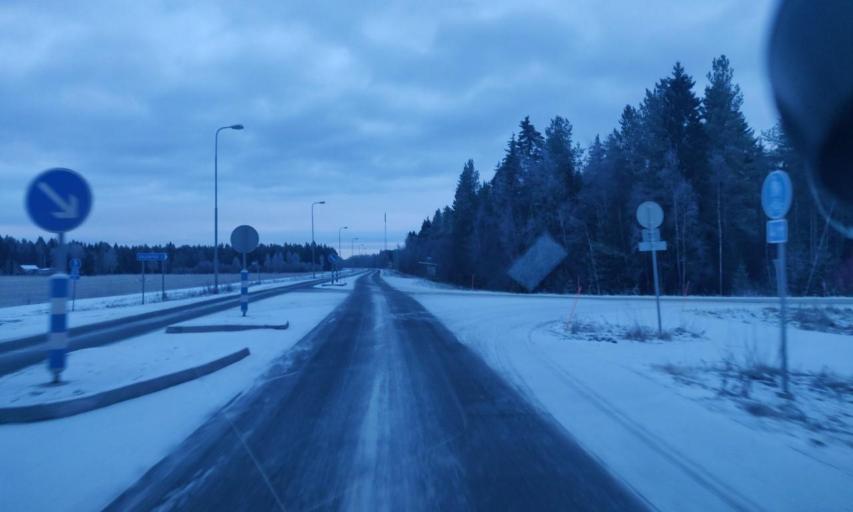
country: FI
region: Northern Ostrobothnia
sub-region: Oulu
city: Oulunsalo
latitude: 64.9791
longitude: 25.2762
